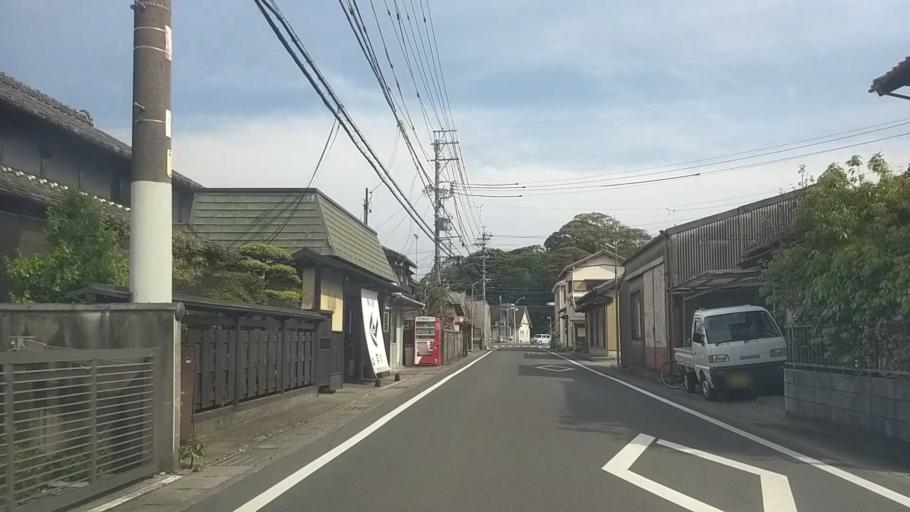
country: JP
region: Shizuoka
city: Kosai-shi
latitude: 34.7052
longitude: 137.6289
